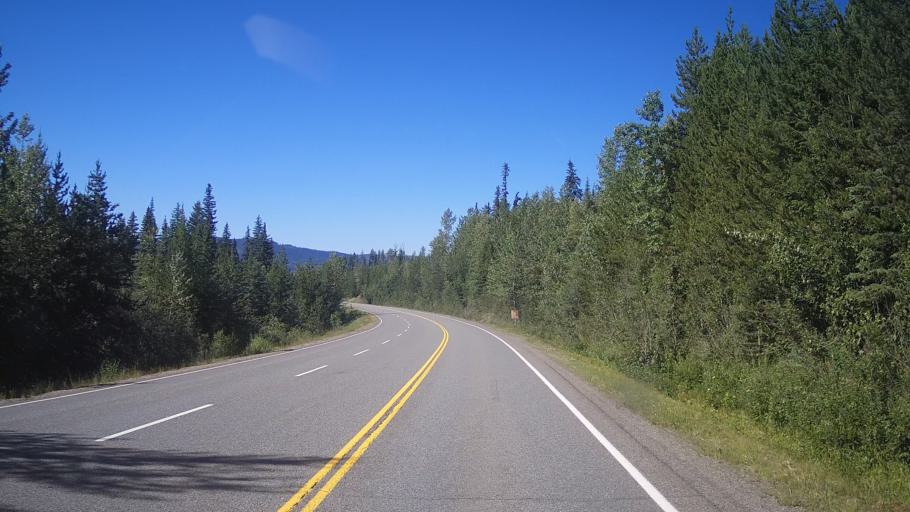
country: CA
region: British Columbia
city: Kamloops
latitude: 51.4900
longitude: -120.4593
